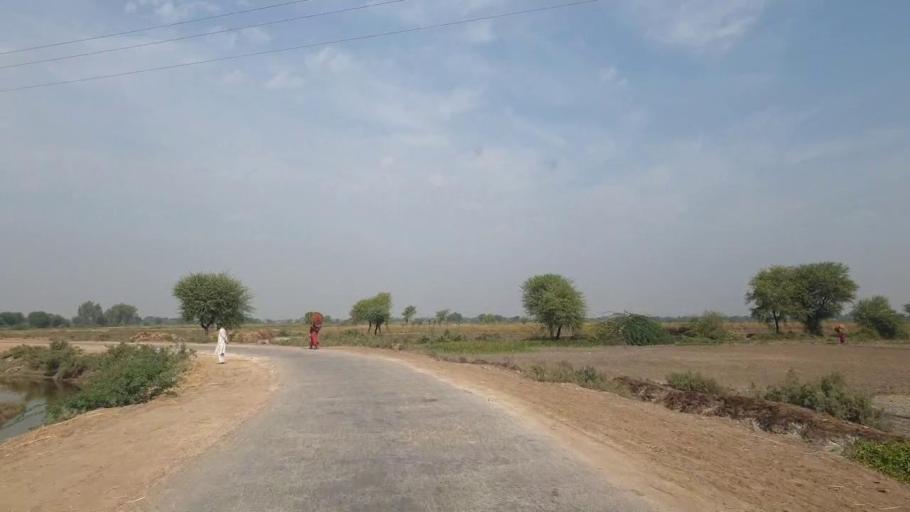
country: PK
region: Sindh
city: Rajo Khanani
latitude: 24.9398
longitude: 68.9841
